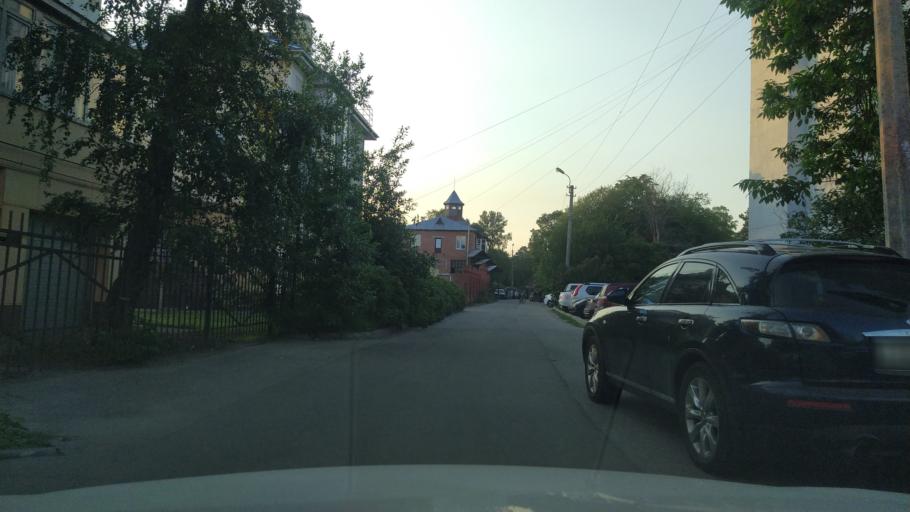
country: RU
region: St.-Petersburg
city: Sestroretsk
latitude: 60.0917
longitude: 29.9481
